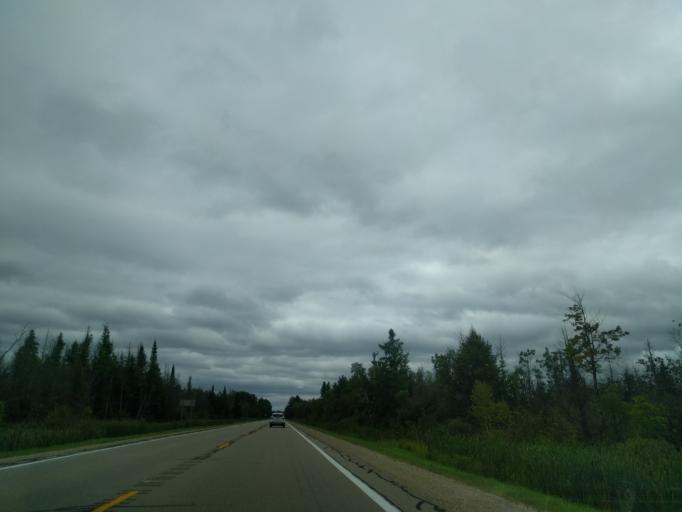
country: US
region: Michigan
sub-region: Menominee County
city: Menominee
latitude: 45.3937
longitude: -87.3686
